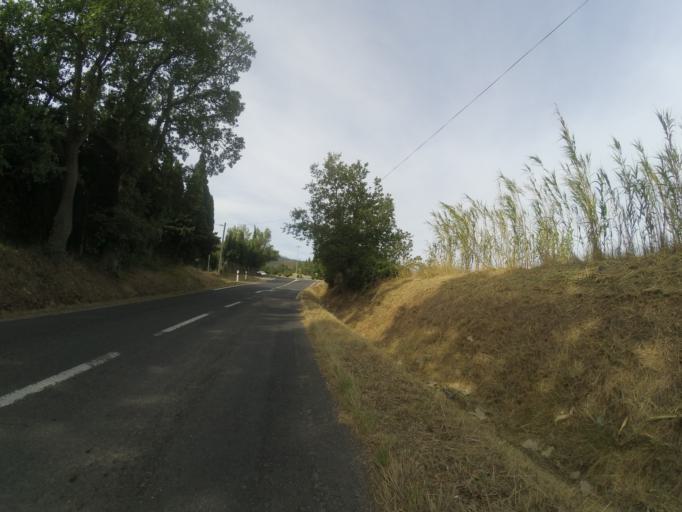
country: FR
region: Languedoc-Roussillon
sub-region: Departement des Pyrenees-Orientales
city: Millas
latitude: 42.6598
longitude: 2.6842
